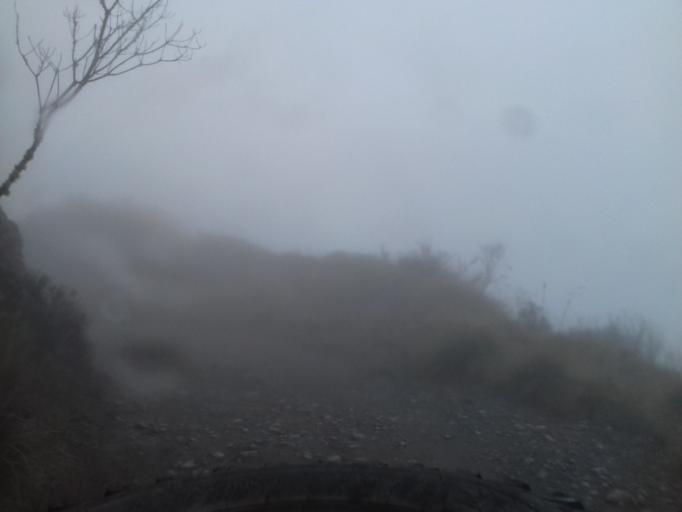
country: CO
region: Tolima
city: Murillo
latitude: 4.9204
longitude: -75.2724
